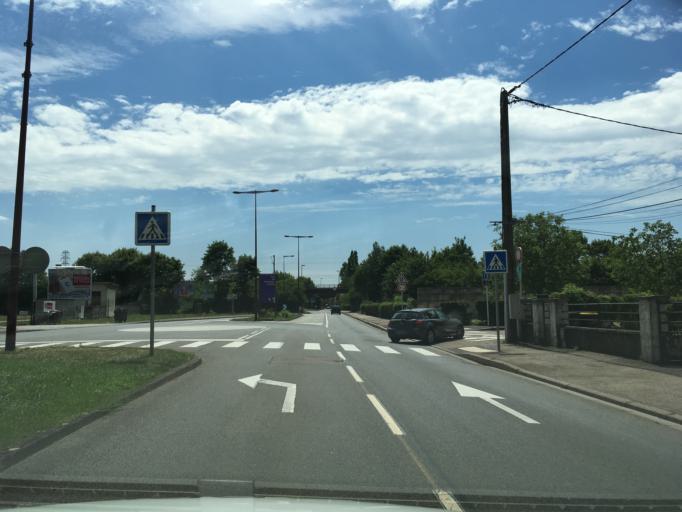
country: FR
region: Lorraine
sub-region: Departement de la Moselle
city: Metz
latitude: 49.1374
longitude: 6.1726
